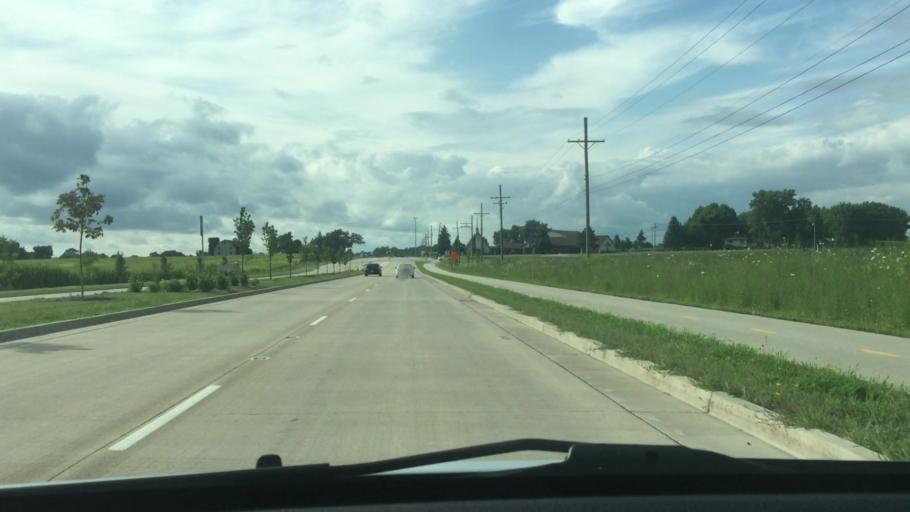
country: US
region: Illinois
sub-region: McHenry County
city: Lakewood
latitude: 42.2650
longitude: -88.3764
